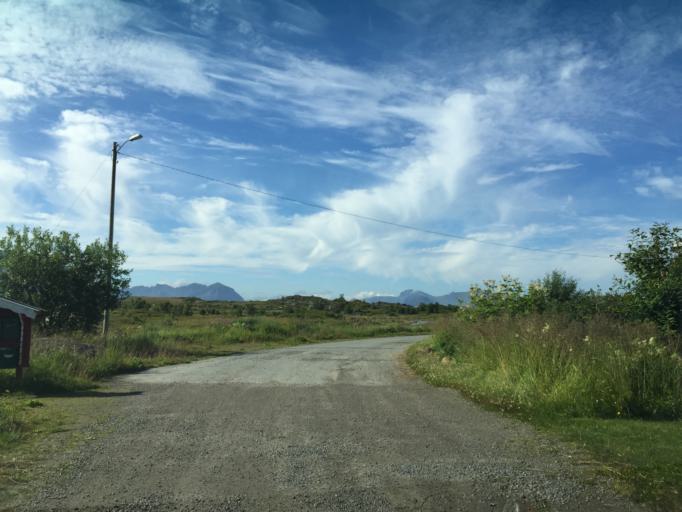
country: NO
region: Nordland
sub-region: Vagan
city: Kabelvag
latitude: 68.3868
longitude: 14.4294
